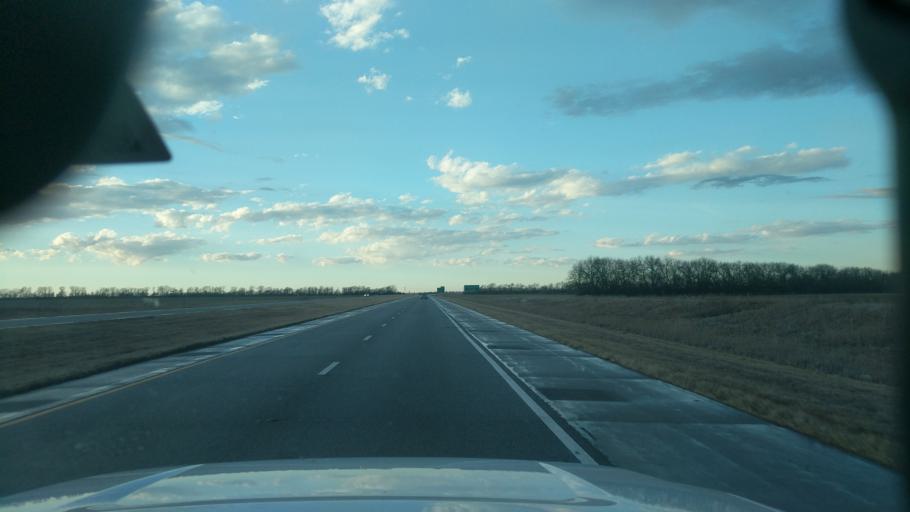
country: US
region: Kansas
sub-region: McPherson County
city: Moundridge
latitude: 38.1902
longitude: -97.4713
